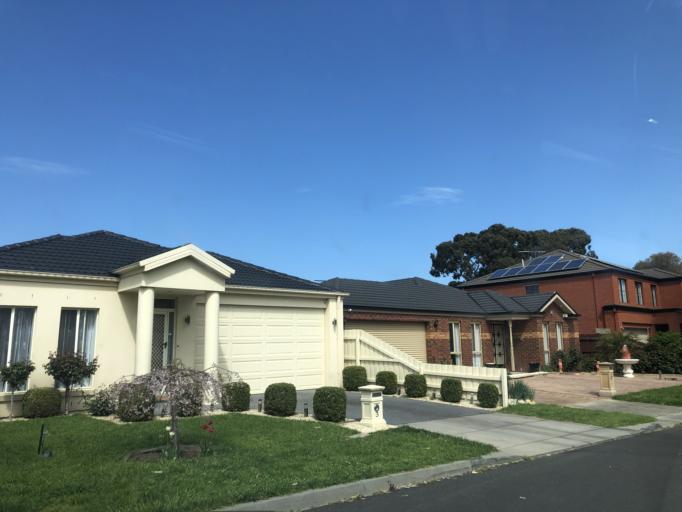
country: AU
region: Victoria
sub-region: Casey
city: Hampton Park
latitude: -38.0460
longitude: 145.2474
